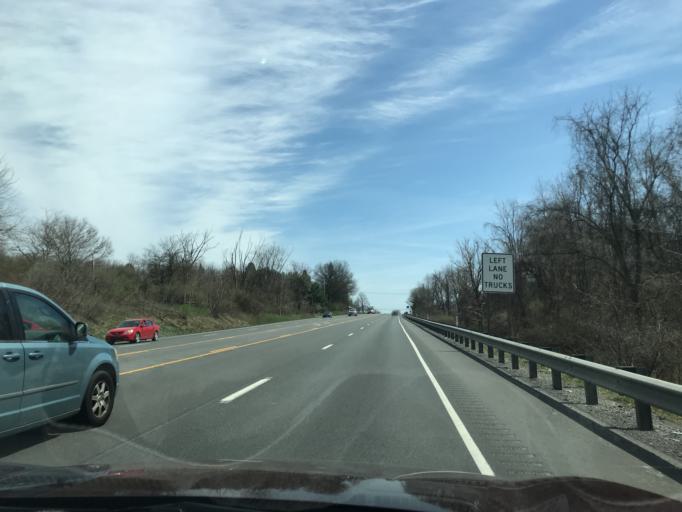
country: US
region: Pennsylvania
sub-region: Union County
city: Lewisburg
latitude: 40.9391
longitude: -76.8766
